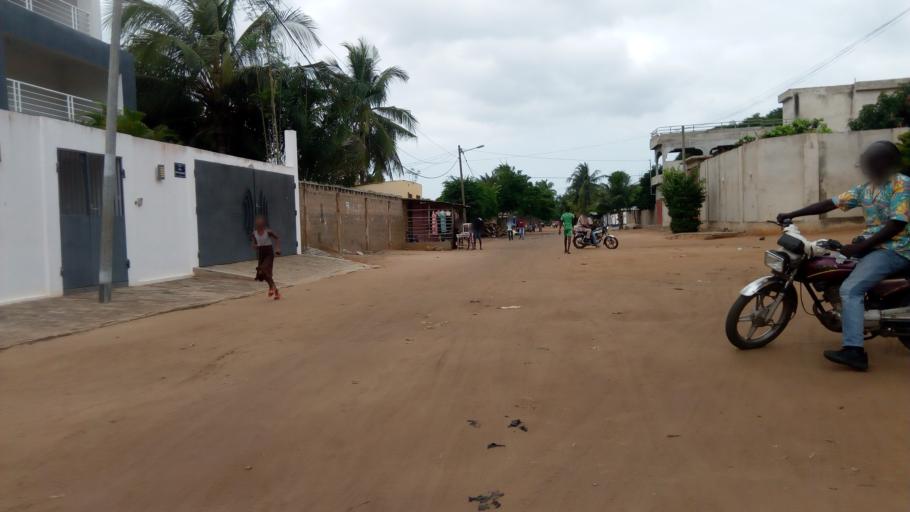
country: TG
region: Maritime
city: Lome
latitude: 6.1730
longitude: 1.1799
